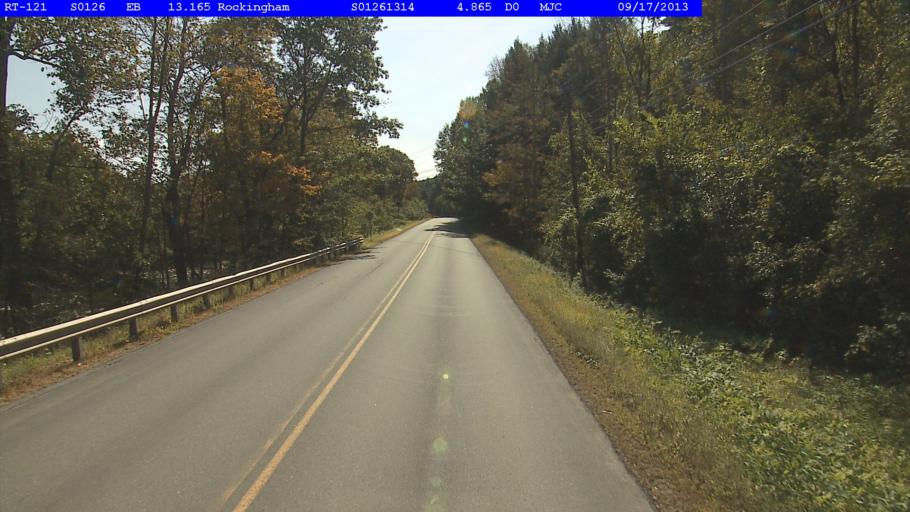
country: US
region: Vermont
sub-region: Windham County
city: Bellows Falls
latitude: 43.1297
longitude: -72.4807
